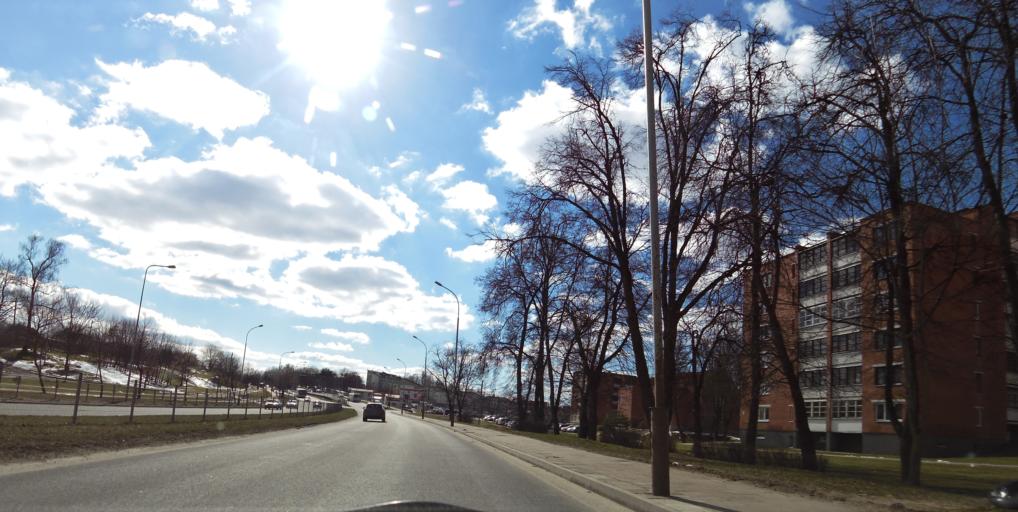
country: LT
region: Vilnius County
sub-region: Vilnius
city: Fabijoniskes
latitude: 54.7421
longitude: 25.2766
